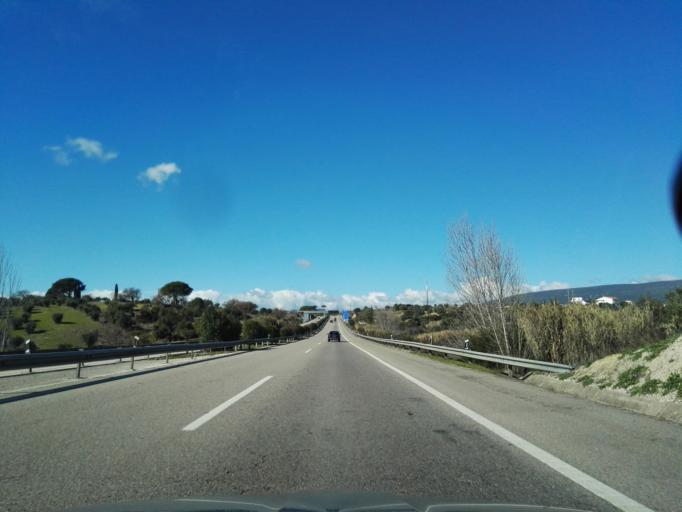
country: PT
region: Santarem
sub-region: Torres Novas
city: Torres Novas
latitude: 39.4696
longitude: -8.5691
